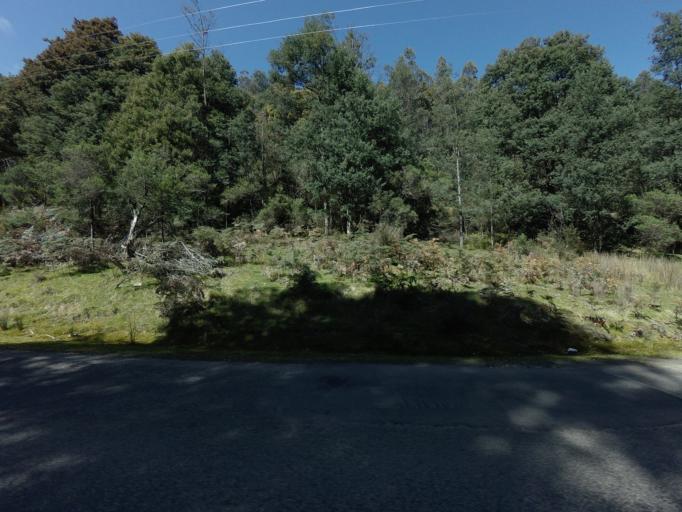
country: AU
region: Tasmania
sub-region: Derwent Valley
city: New Norfolk
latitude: -42.7616
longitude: 146.6060
